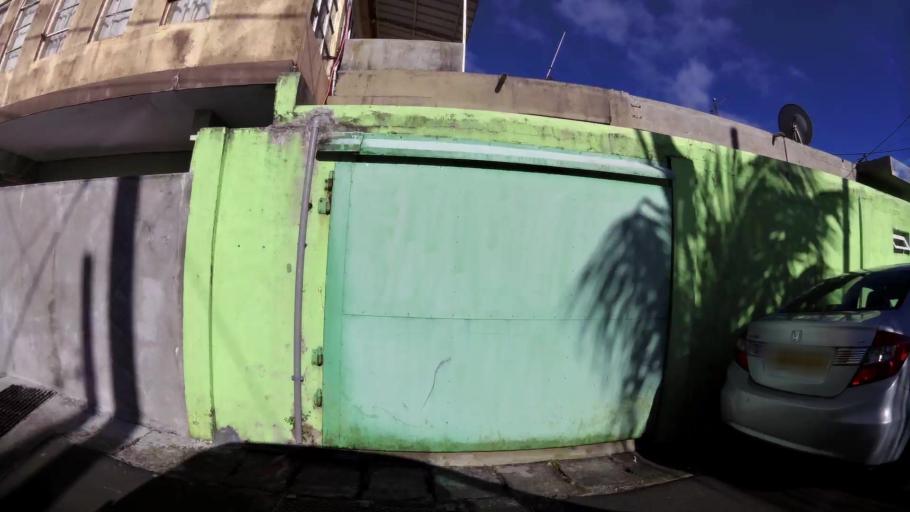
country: MU
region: Plaines Wilhems
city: Curepipe
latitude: -20.3199
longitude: 57.5352
